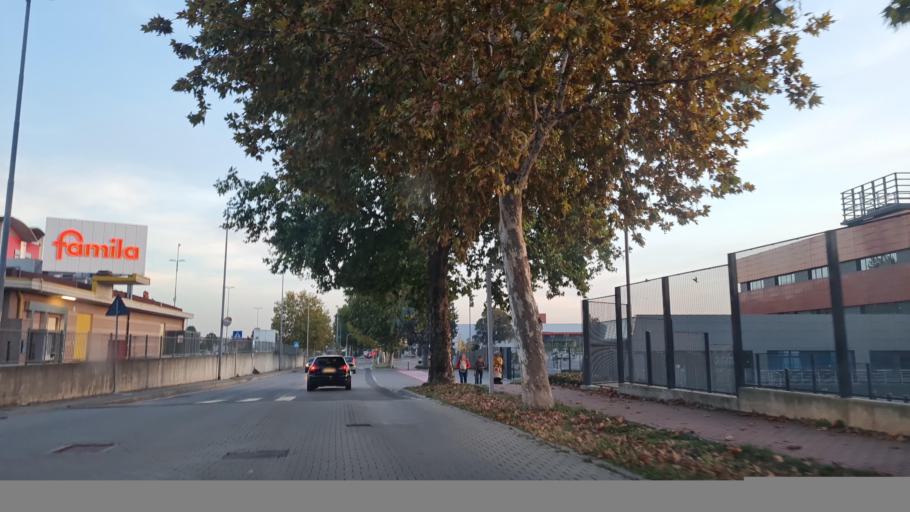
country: IT
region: Lombardy
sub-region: Provincia di Bergamo
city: Ponte San Pietro
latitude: 45.7070
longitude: 9.5903
